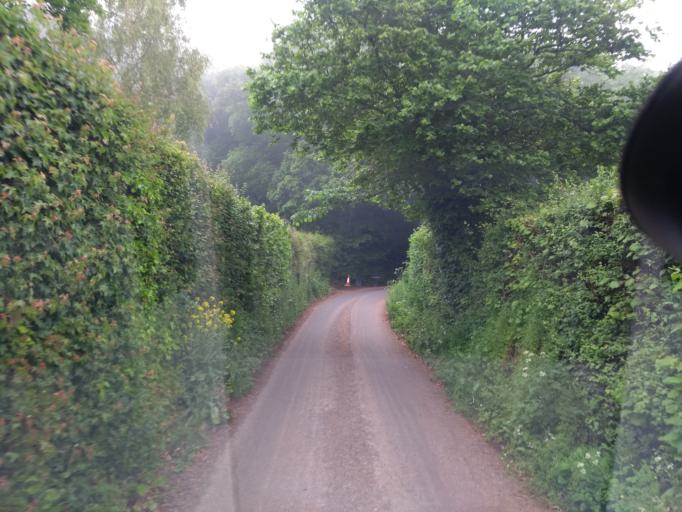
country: GB
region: England
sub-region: Somerset
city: Creech Saint Michael
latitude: 50.9858
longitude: -2.9976
